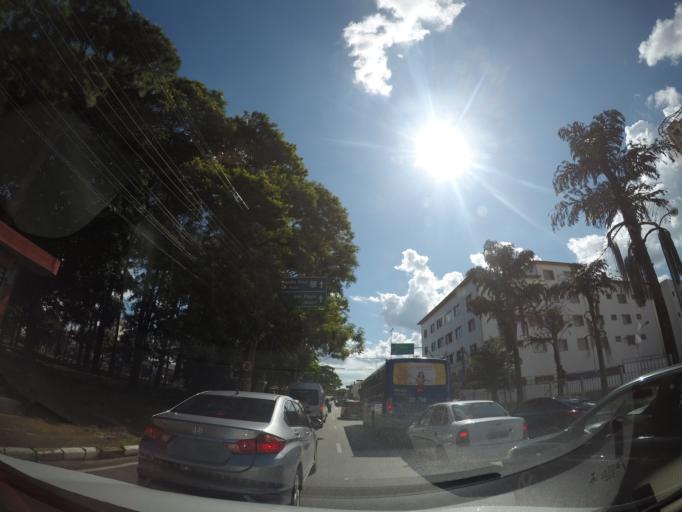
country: BR
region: Sao Paulo
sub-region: Guarulhos
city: Guarulhos
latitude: -23.4574
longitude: -46.5669
